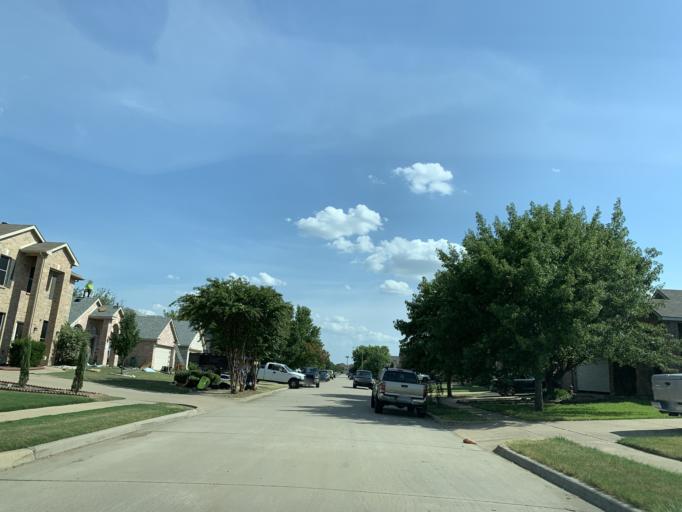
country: US
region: Texas
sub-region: Dallas County
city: Cedar Hill
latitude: 32.6515
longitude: -97.0103
